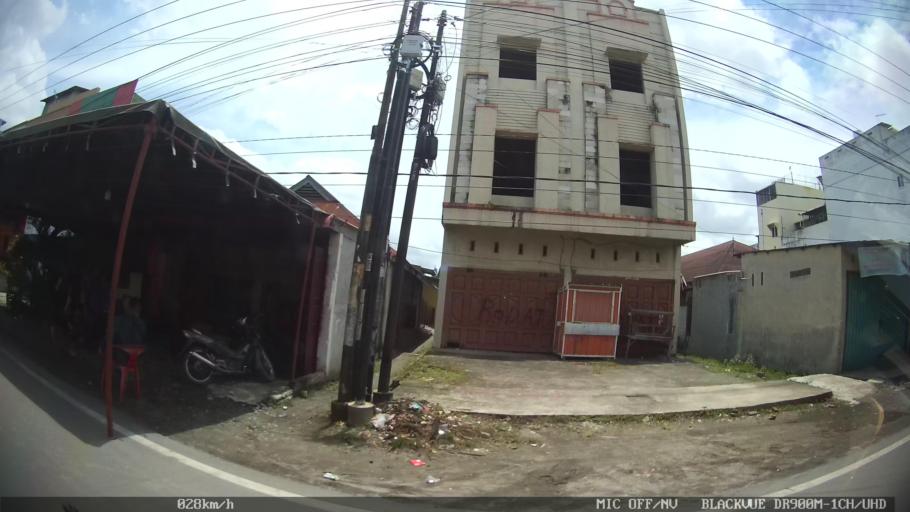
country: ID
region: North Sumatra
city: Medan
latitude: 3.6156
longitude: 98.7052
